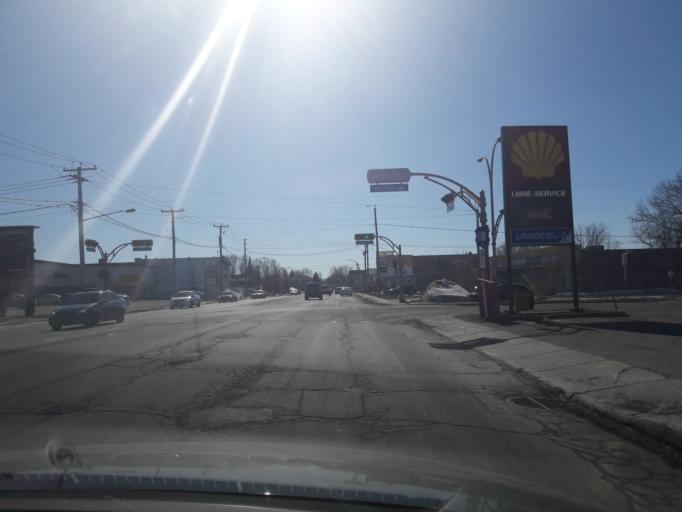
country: CA
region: Quebec
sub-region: Laval
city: Laval
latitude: 45.5529
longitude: -73.7575
